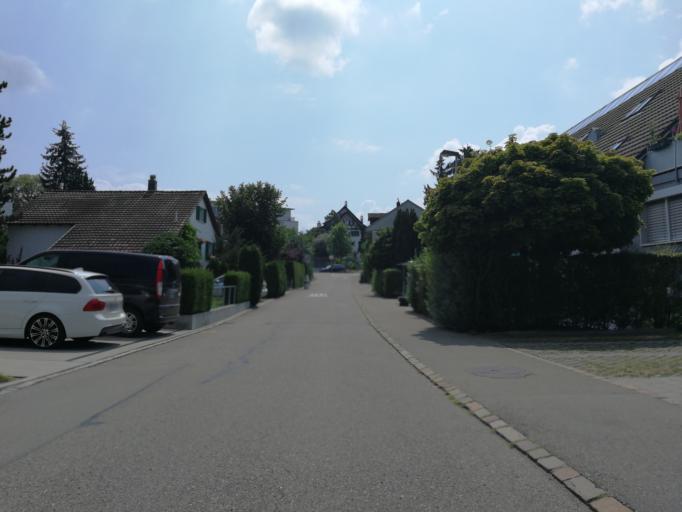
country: CH
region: Zurich
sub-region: Bezirk Hinwil
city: Gossau
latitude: 47.3028
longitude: 8.7653
